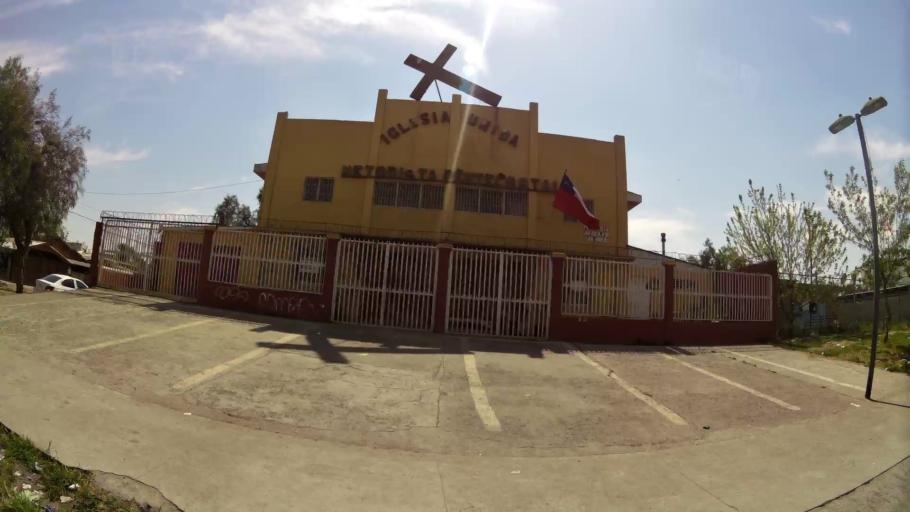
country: CL
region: Santiago Metropolitan
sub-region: Provincia de Santiago
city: La Pintana
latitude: -33.5529
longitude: -70.6413
